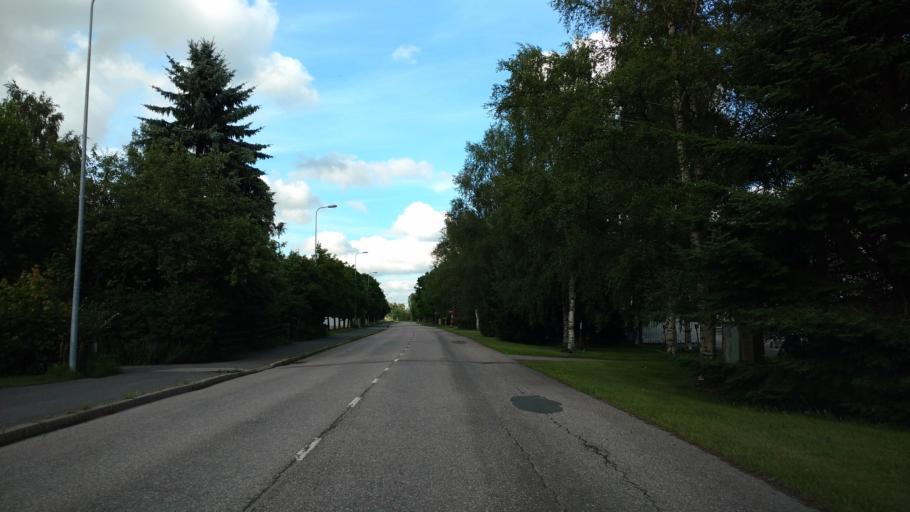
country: FI
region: Varsinais-Suomi
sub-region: Salo
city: Salo
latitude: 60.3981
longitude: 23.1450
